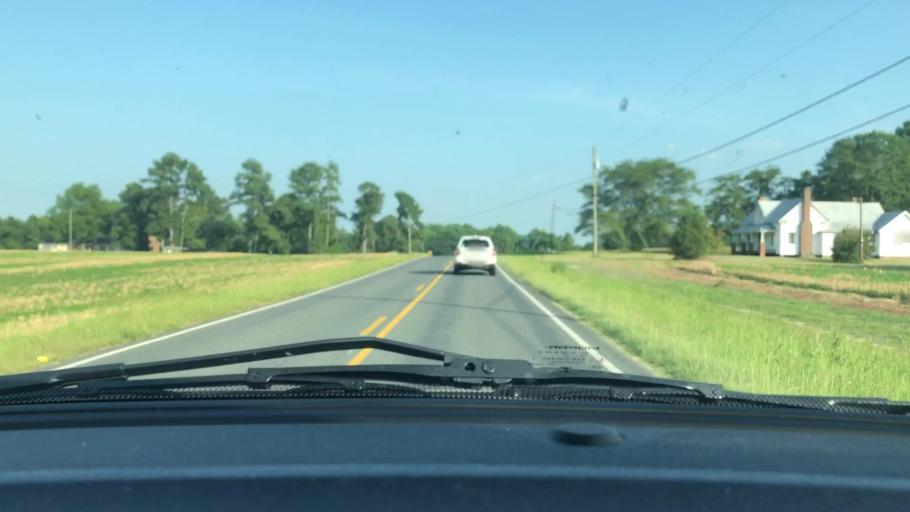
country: US
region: North Carolina
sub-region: Lee County
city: Broadway
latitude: 35.3653
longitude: -79.0930
